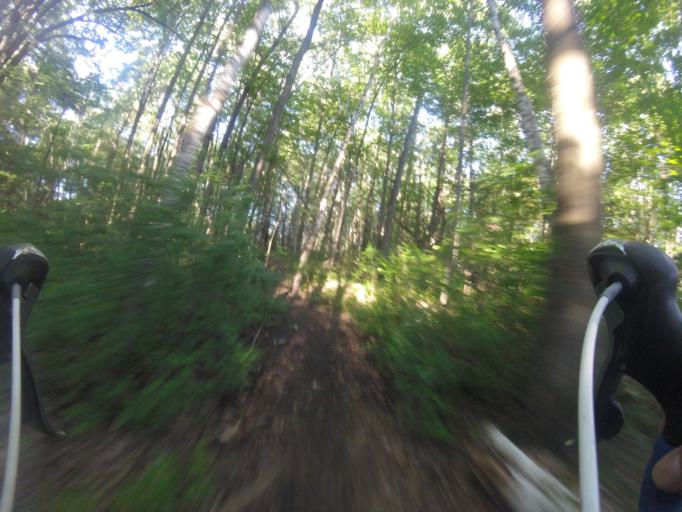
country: CA
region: Ontario
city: Bells Corners
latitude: 45.3212
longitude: -75.8026
